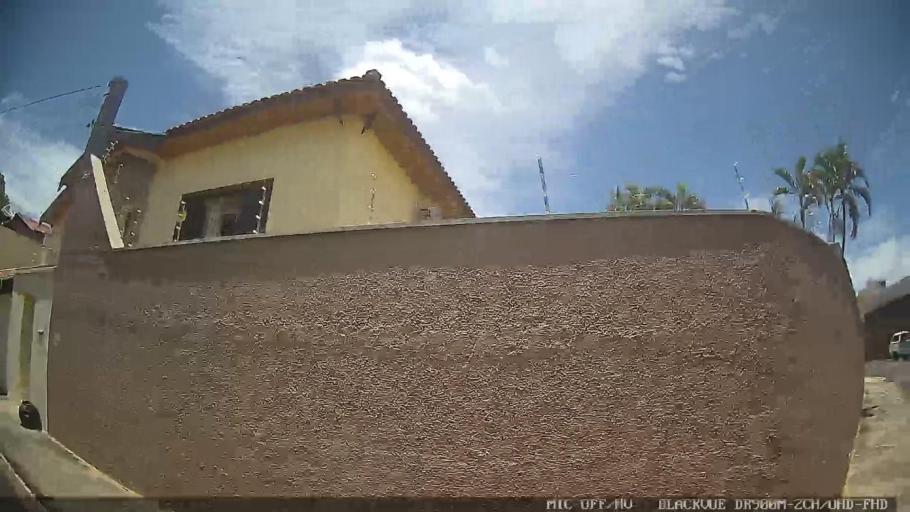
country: BR
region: Sao Paulo
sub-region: Laranjal Paulista
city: Laranjal Paulista
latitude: -23.0474
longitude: -47.8341
